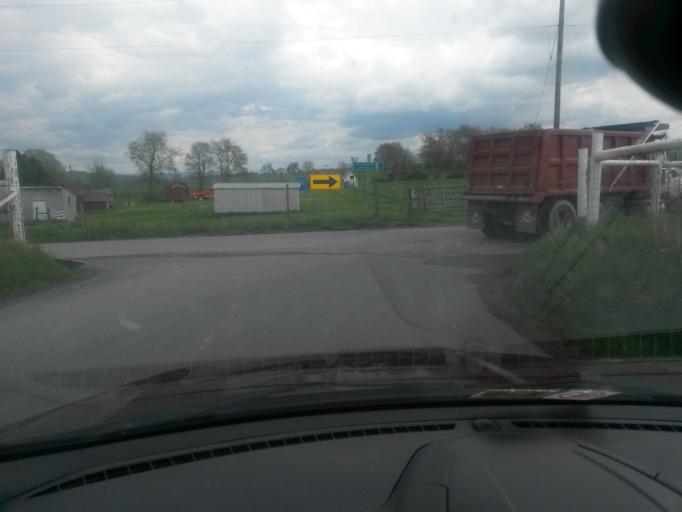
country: US
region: West Virginia
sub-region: Greenbrier County
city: Lewisburg
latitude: 37.8968
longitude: -80.4127
